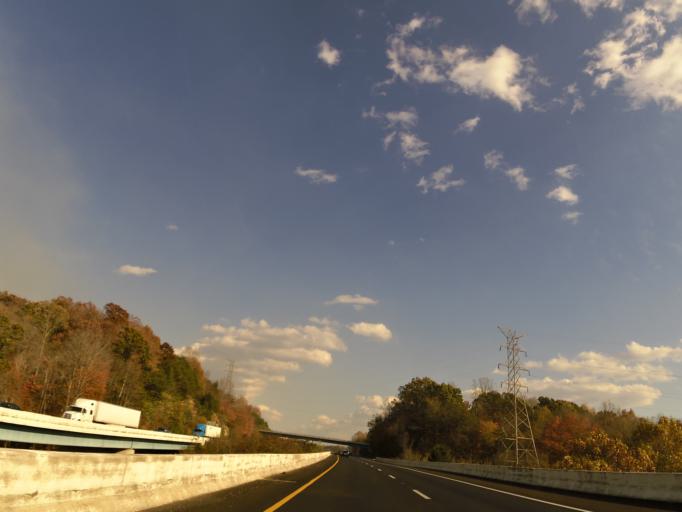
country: US
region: Tennessee
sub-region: Anderson County
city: Rocky Top
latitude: 36.2124
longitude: -84.1376
